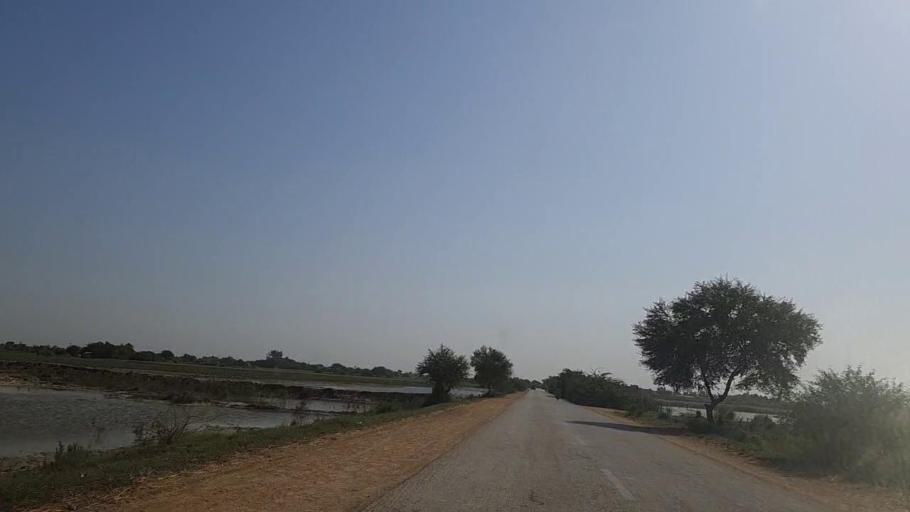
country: PK
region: Sindh
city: Mirpur Batoro
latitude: 24.6114
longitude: 68.2959
